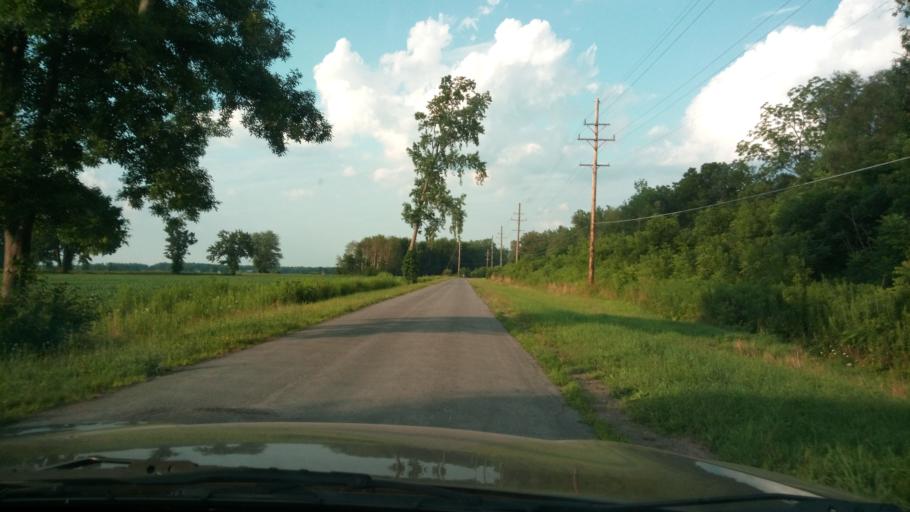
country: US
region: New York
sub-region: Wayne County
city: Clyde
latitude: 43.0853
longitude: -76.9145
